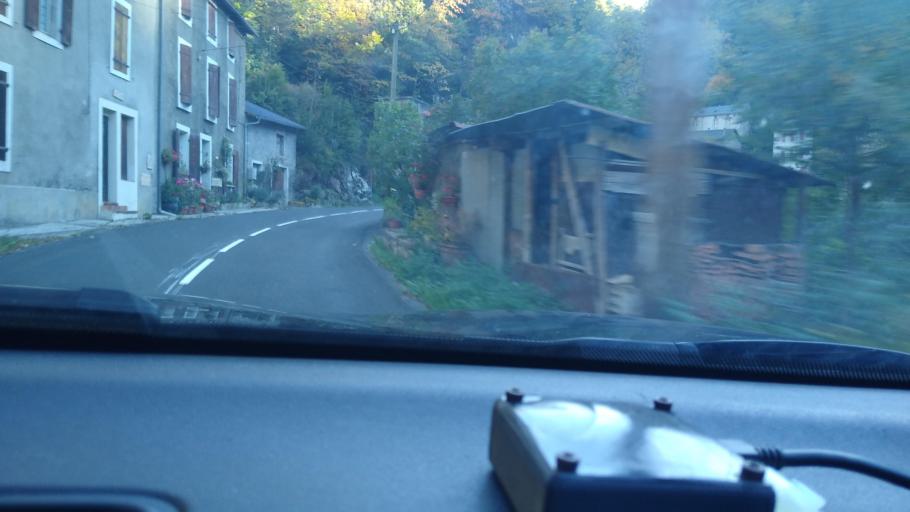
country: FR
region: Languedoc-Roussillon
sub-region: Departement de l'Aude
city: Quillan
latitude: 42.7211
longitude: 2.1212
